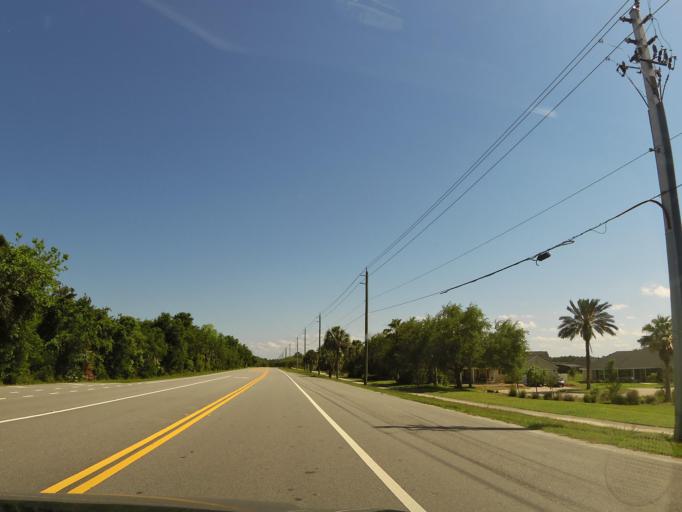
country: US
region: Florida
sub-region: Flagler County
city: Flagler Beach
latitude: 29.4233
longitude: -81.1507
